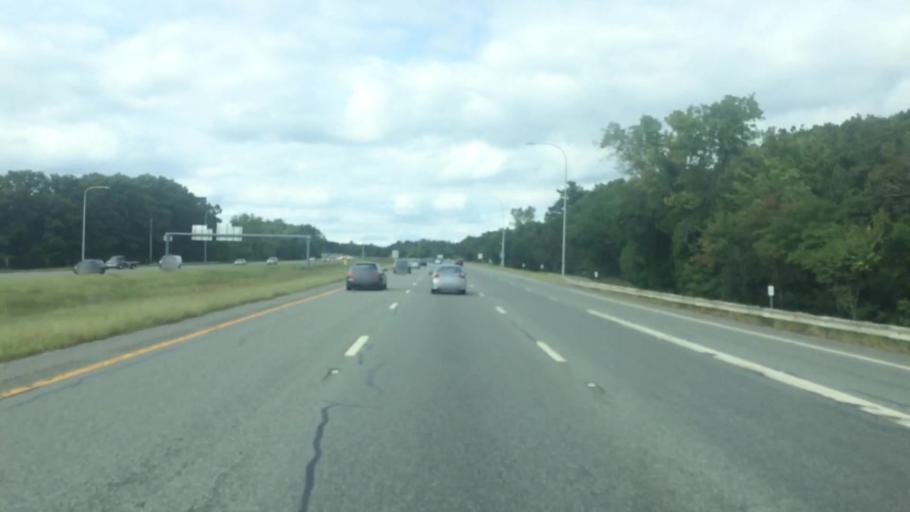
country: US
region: Rhode Island
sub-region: Providence County
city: Greenville
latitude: 41.8727
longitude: -71.5148
